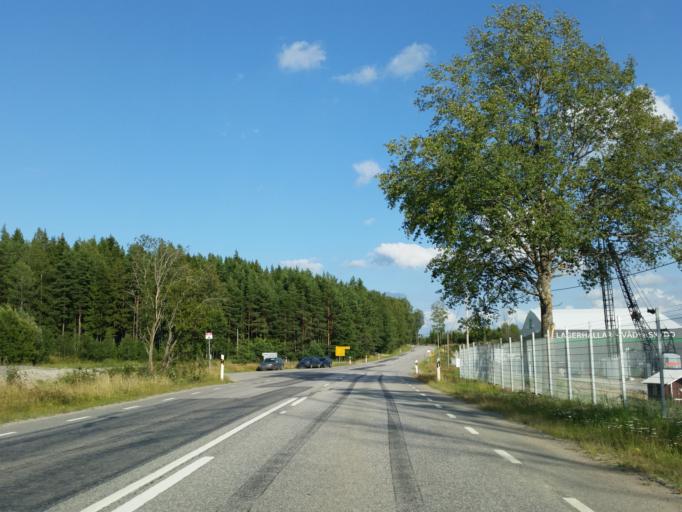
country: SE
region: Stockholm
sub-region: Nykvarns Kommun
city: Nykvarn
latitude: 59.2087
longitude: 17.3554
